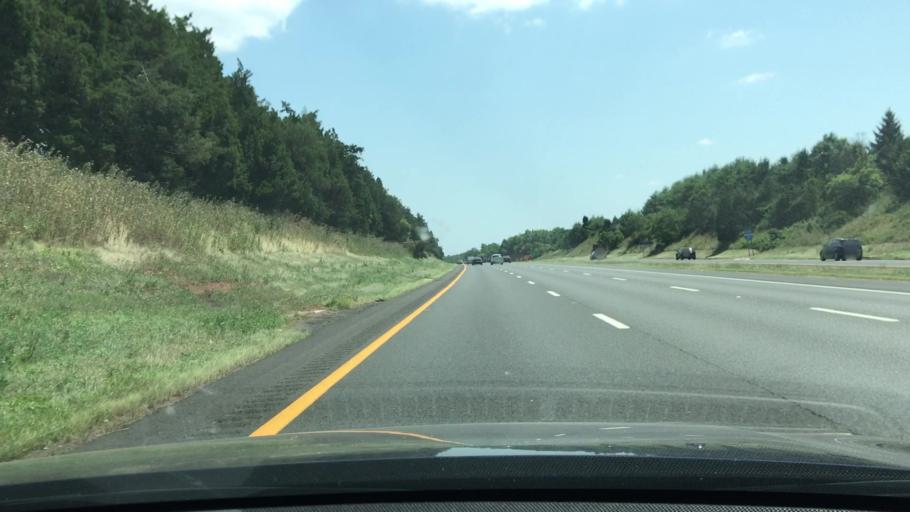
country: US
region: New Jersey
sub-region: Somerset County
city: Bridgewater
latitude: 40.6259
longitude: -74.6411
